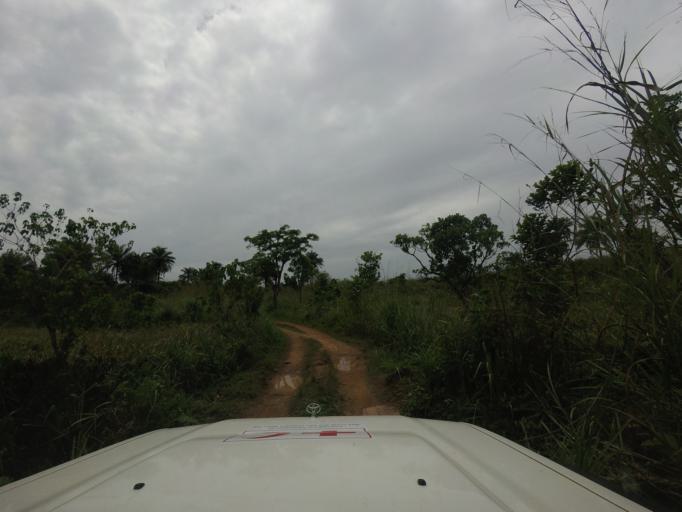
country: SL
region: Eastern Province
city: Buedu
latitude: 8.4254
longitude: -10.2616
